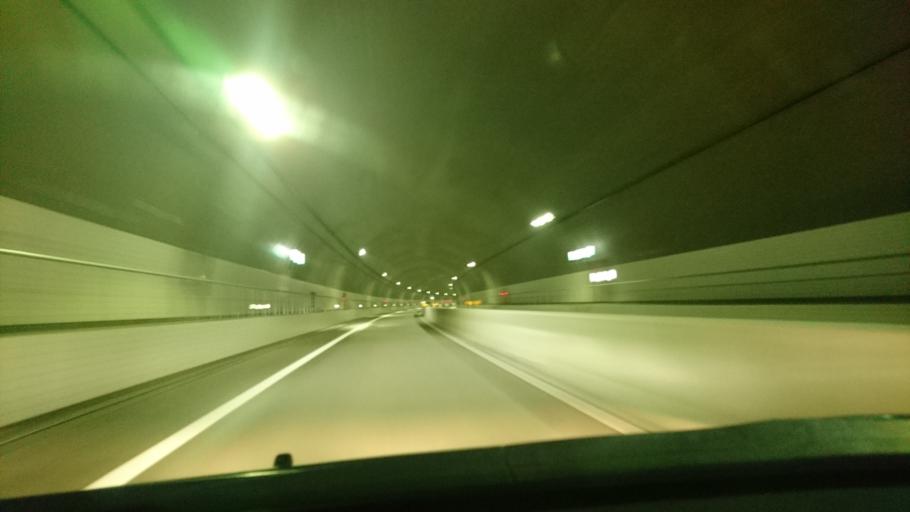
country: JP
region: Iwate
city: Miyako
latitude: 39.8099
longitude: 141.9570
